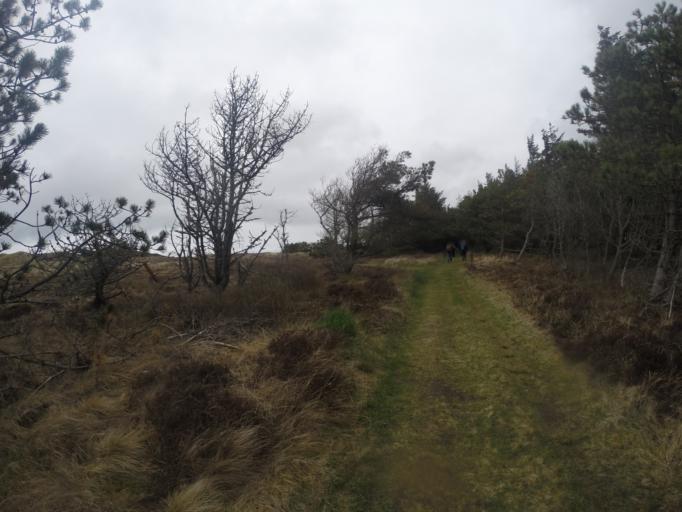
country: DK
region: North Denmark
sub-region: Thisted Kommune
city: Hurup
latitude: 56.9144
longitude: 8.3546
